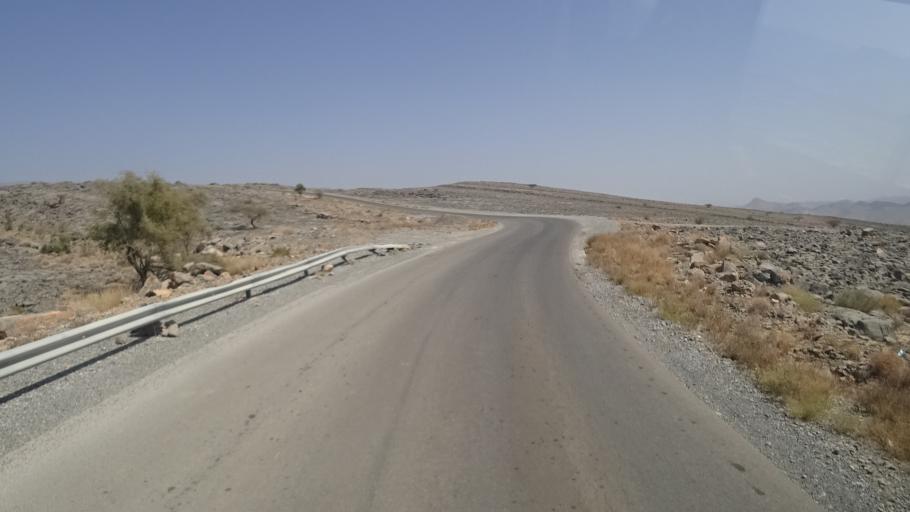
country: OM
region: Muhafazat ad Dakhiliyah
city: Bahla'
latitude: 23.1026
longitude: 57.3513
